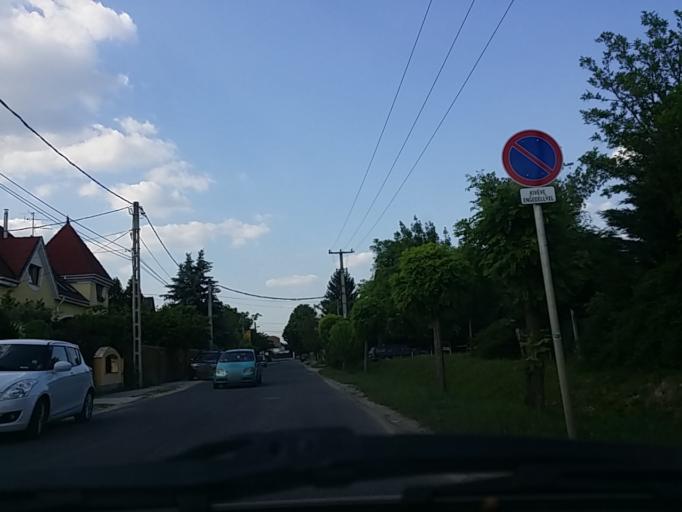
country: HU
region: Pest
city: Budakalasz
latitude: 47.6191
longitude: 19.0593
